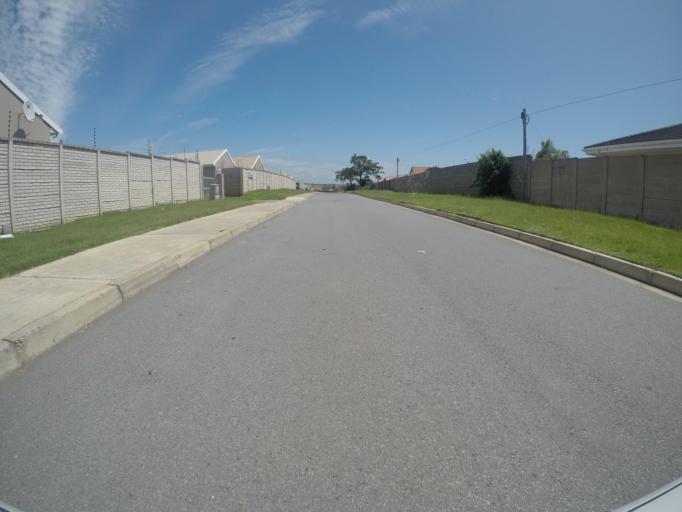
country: ZA
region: Eastern Cape
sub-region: Buffalo City Metropolitan Municipality
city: East London
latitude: -32.9529
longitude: 27.9964
